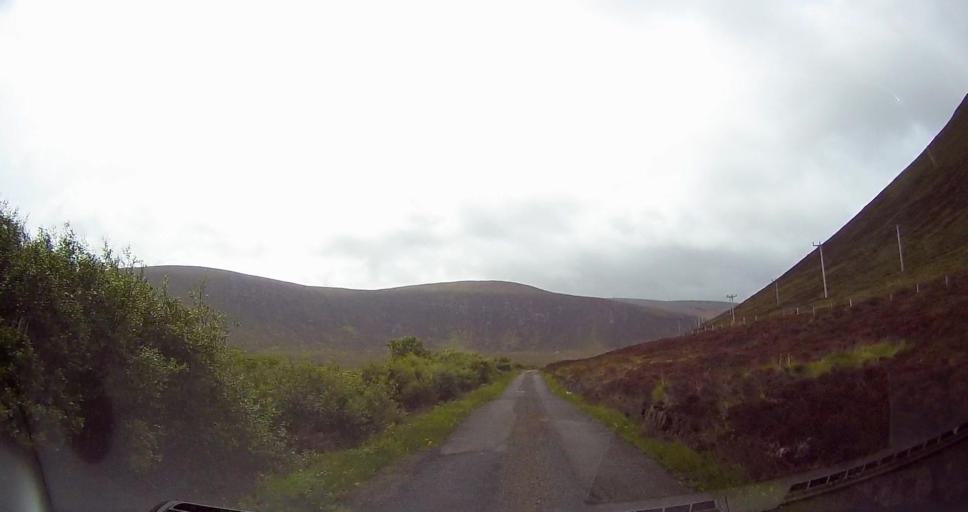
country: GB
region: Scotland
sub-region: Orkney Islands
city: Stromness
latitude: 58.8962
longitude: -3.3145
